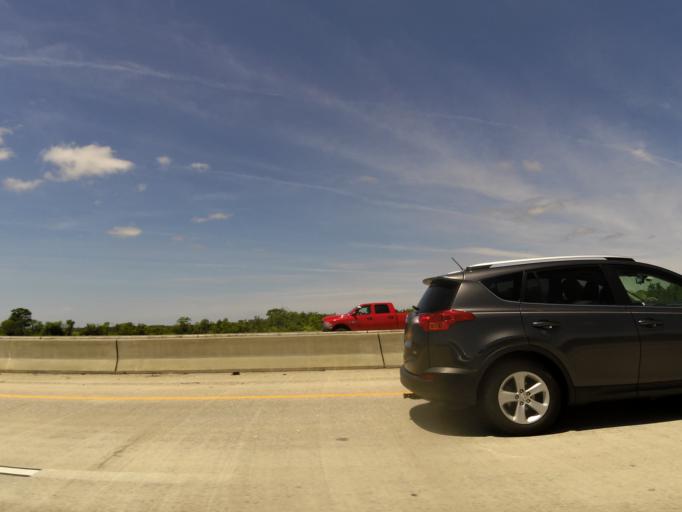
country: US
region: Georgia
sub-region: McIntosh County
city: Darien
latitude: 31.3652
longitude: -81.4571
